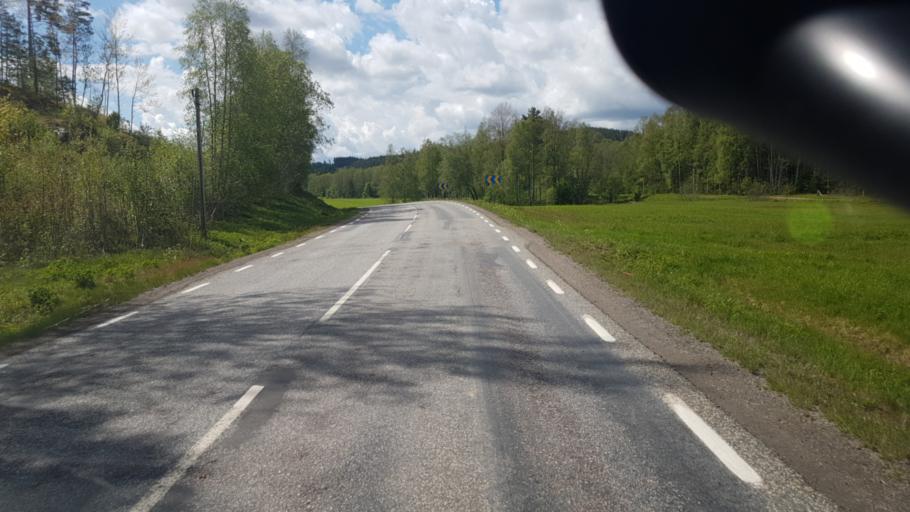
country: SE
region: Vaermland
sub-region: Arjangs Kommun
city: Arjaeng
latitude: 59.5829
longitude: 12.1243
